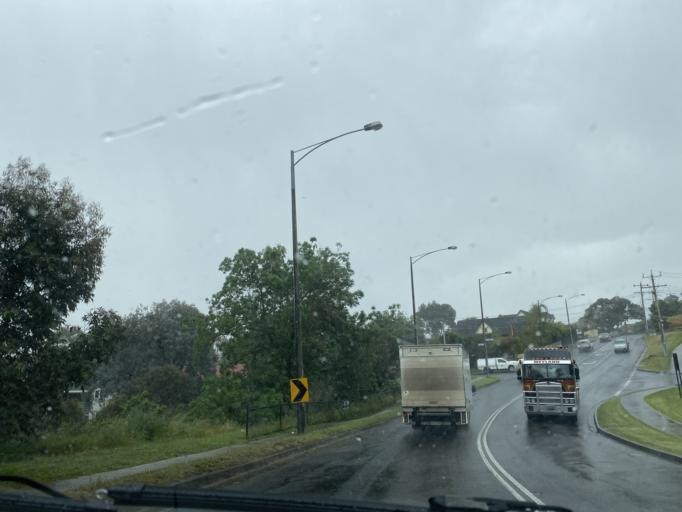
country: AU
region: Victoria
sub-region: Banyule
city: Lower Plenty
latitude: -37.7259
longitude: 145.1120
